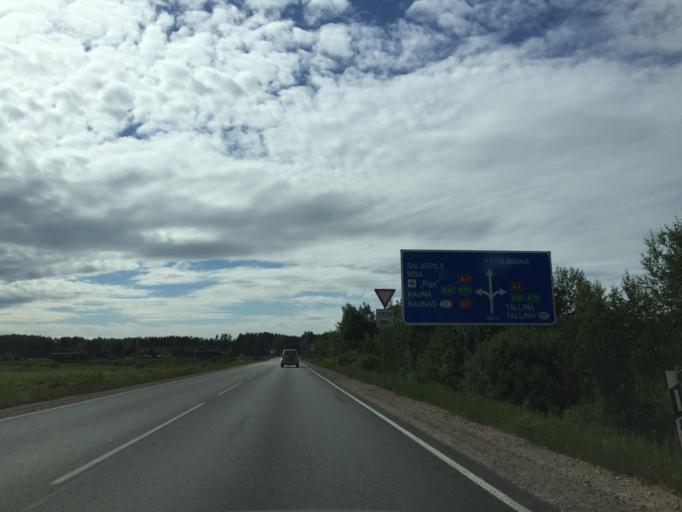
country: LV
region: Salaspils
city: Salaspils
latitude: 56.9001
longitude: 24.4125
